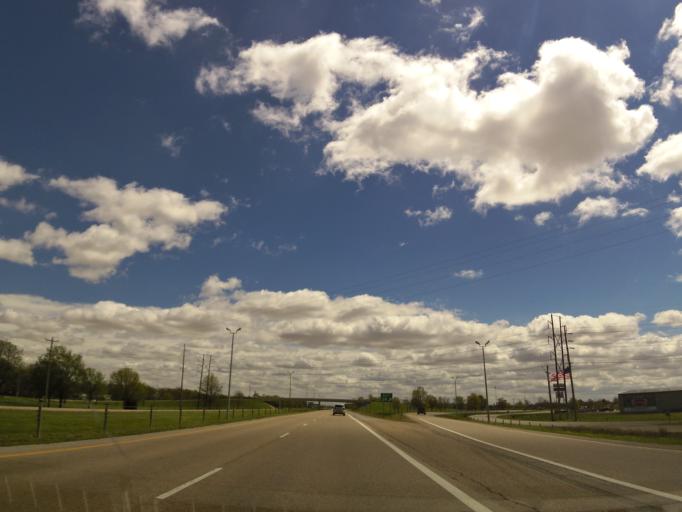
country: US
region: Arkansas
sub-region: Craighead County
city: Jonesboro
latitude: 35.8038
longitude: -90.6281
